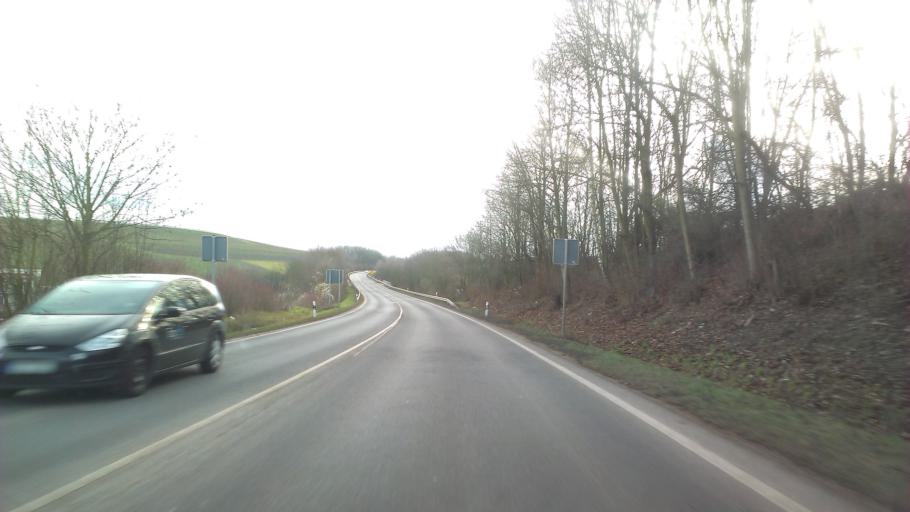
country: DE
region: Rheinland-Pfalz
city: Hackenheim
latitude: 49.8293
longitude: 7.9050
